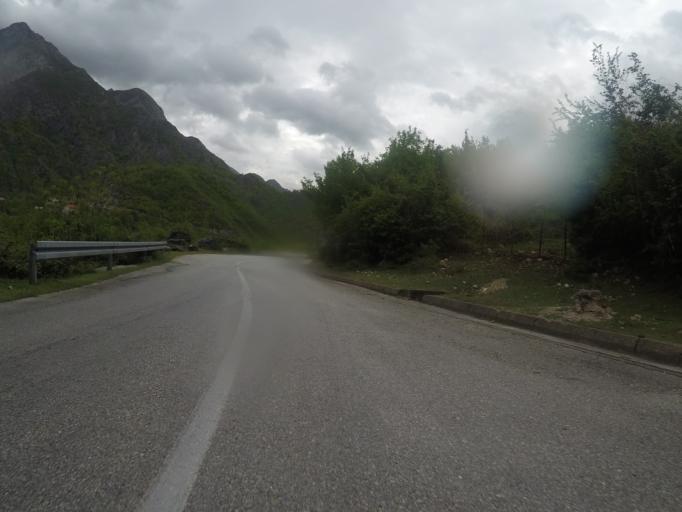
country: BA
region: Federation of Bosnia and Herzegovina
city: Jablanica
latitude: 43.5343
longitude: 17.6597
